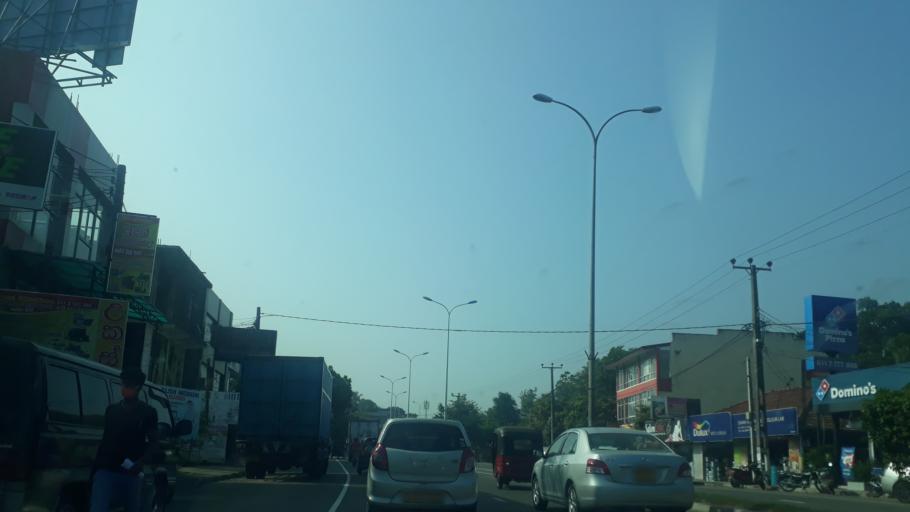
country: LK
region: Western
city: Kelaniya
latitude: 6.9993
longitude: 79.9482
